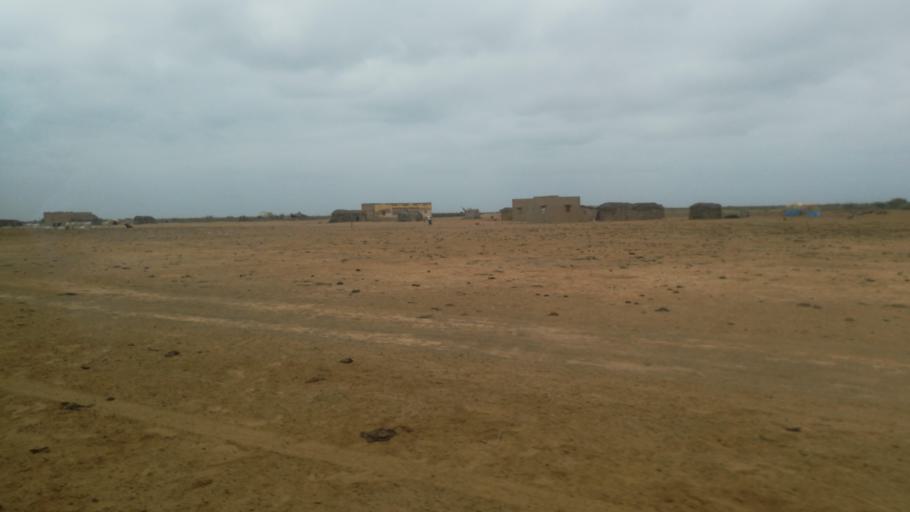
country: SN
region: Saint-Louis
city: Saint-Louis
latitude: 16.3137
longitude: -16.2278
